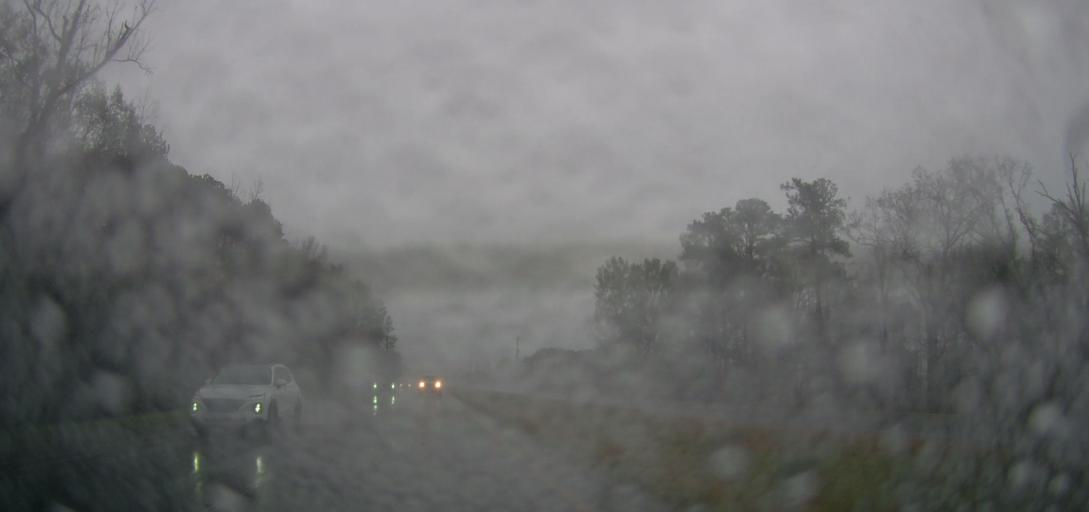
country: US
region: Alabama
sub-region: Autauga County
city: Prattville
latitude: 32.4039
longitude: -86.4040
